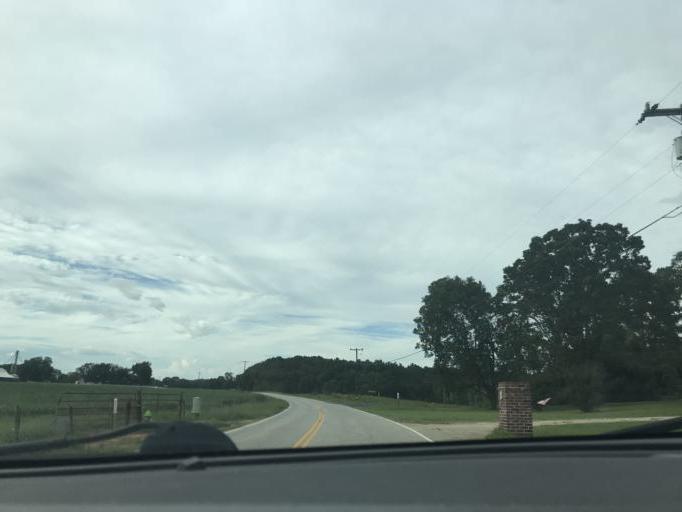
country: US
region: South Carolina
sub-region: Cherokee County
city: East Gaffney
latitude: 35.1153
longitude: -81.6511
